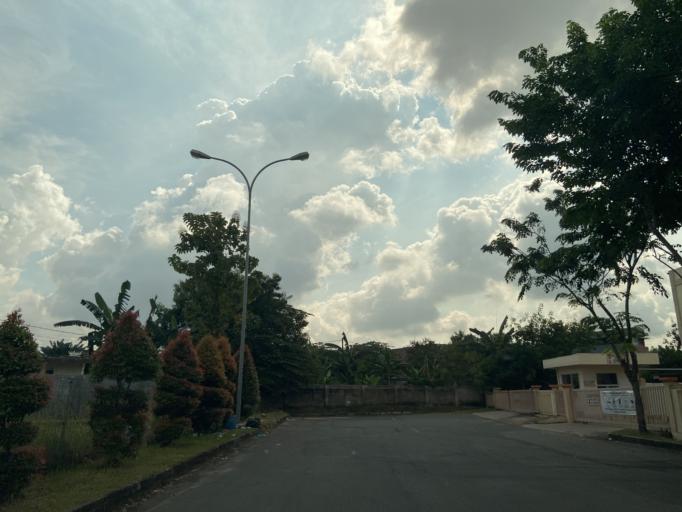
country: SG
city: Singapore
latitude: 1.1110
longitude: 104.0746
